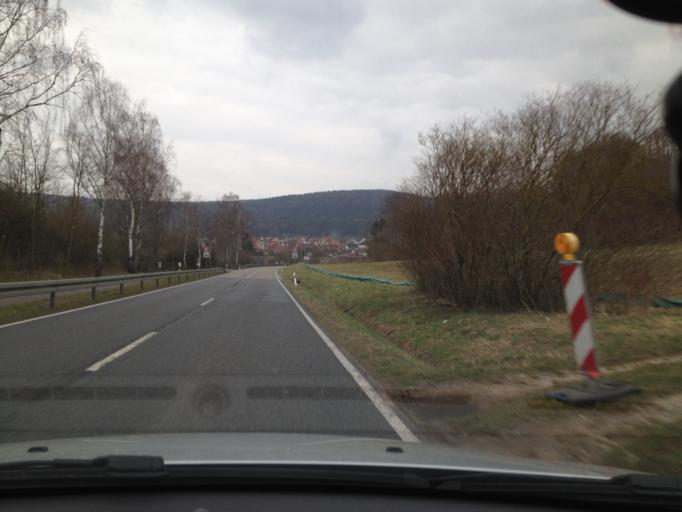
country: DE
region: Bavaria
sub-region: Regierungsbezirk Unterfranken
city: Faulbach
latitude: 49.7837
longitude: 9.4317
